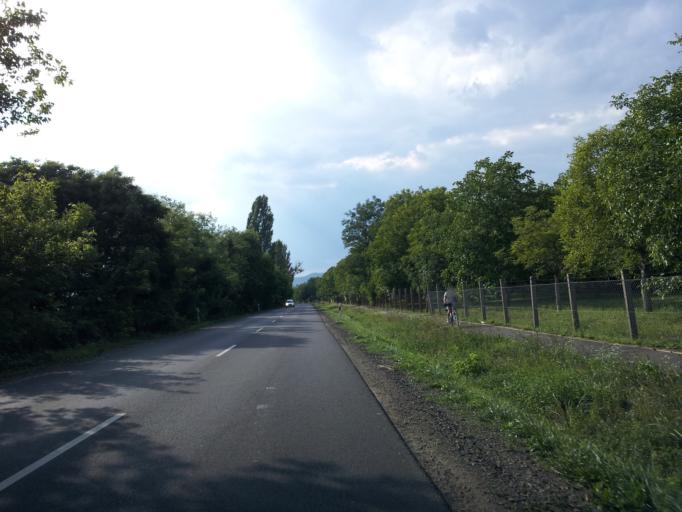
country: HU
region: Pest
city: Veroce
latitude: 47.8194
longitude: 19.0484
